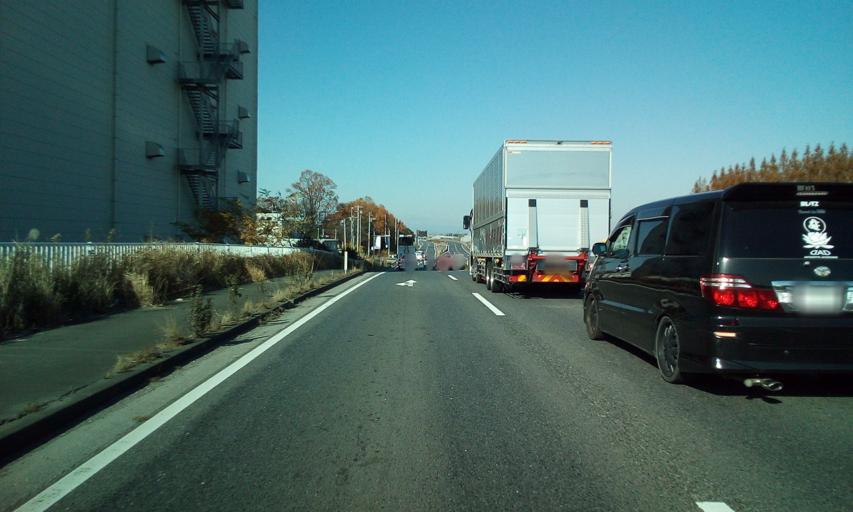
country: JP
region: Ibaraki
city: Sakai
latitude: 36.0818
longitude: 139.7690
